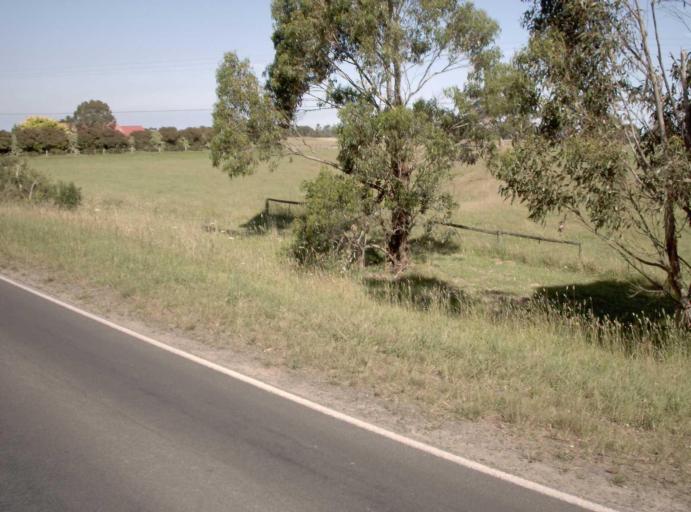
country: AU
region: Victoria
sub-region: Latrobe
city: Traralgon
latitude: -38.5499
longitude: 146.6856
